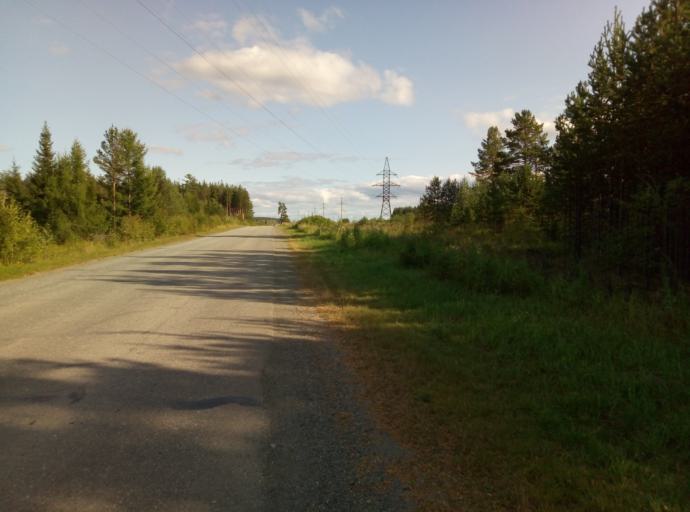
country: RU
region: Sverdlovsk
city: Karpinsk
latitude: 59.8009
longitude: 59.9628
